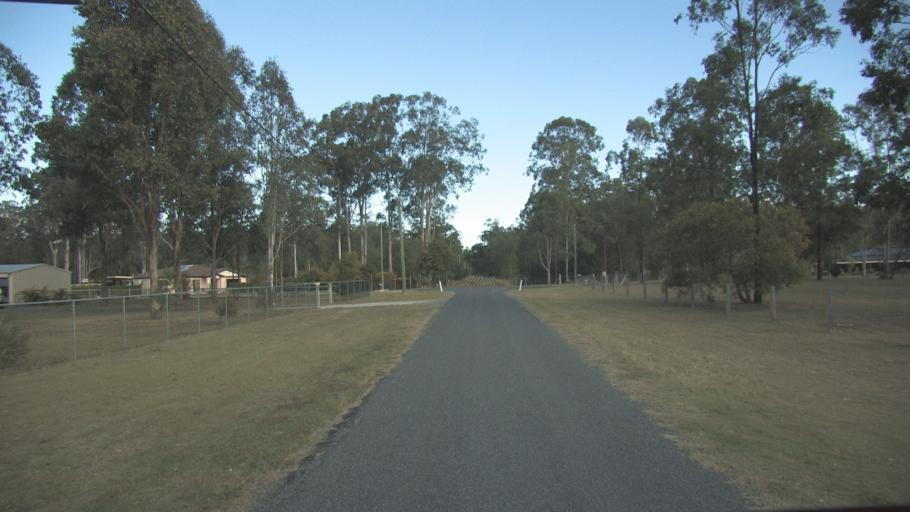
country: AU
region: Queensland
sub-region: Logan
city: North Maclean
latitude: -27.8226
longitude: 153.0487
